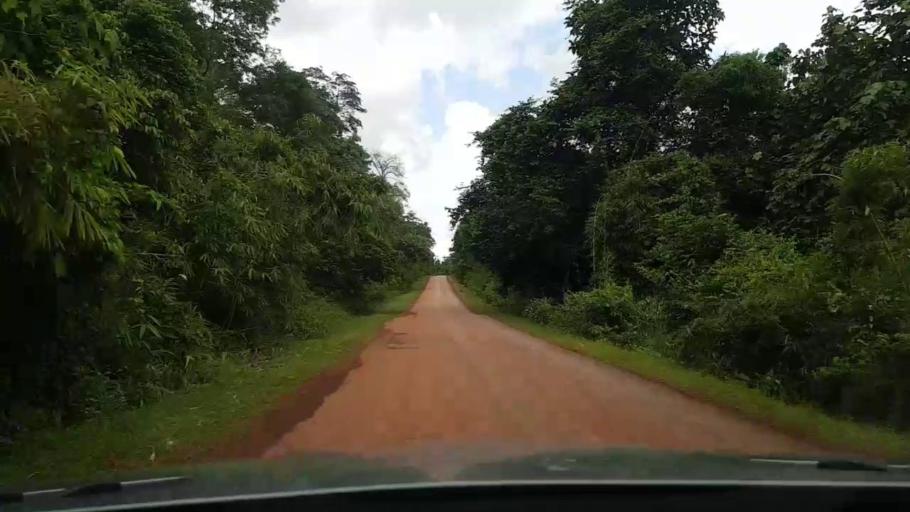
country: MY
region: Pahang
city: Pekan
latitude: 3.1349
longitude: 102.9738
